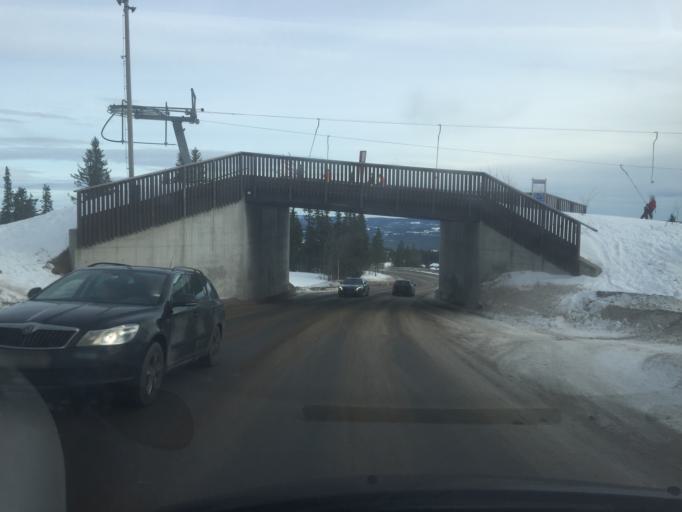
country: NO
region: Hedmark
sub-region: Trysil
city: Innbygda
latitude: 61.3297
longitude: 12.1592
